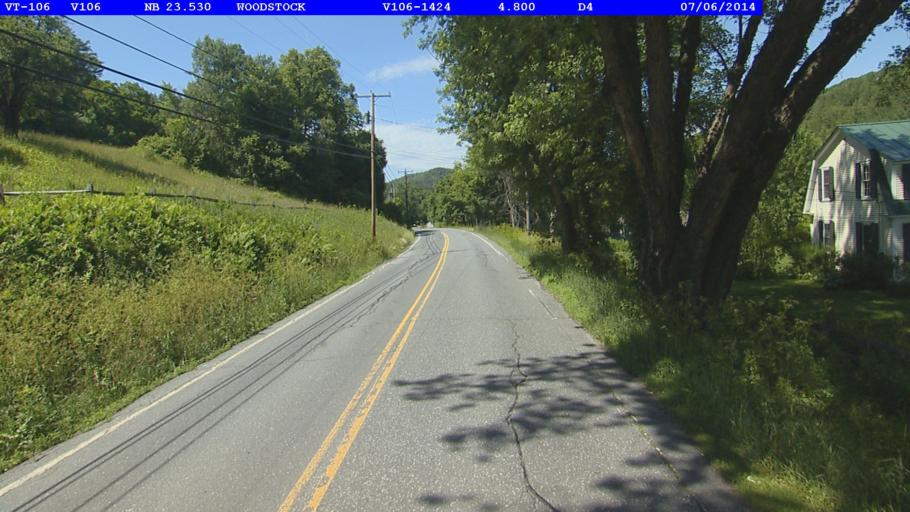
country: US
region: Vermont
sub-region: Windsor County
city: Woodstock
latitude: 43.5900
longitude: -72.5159
